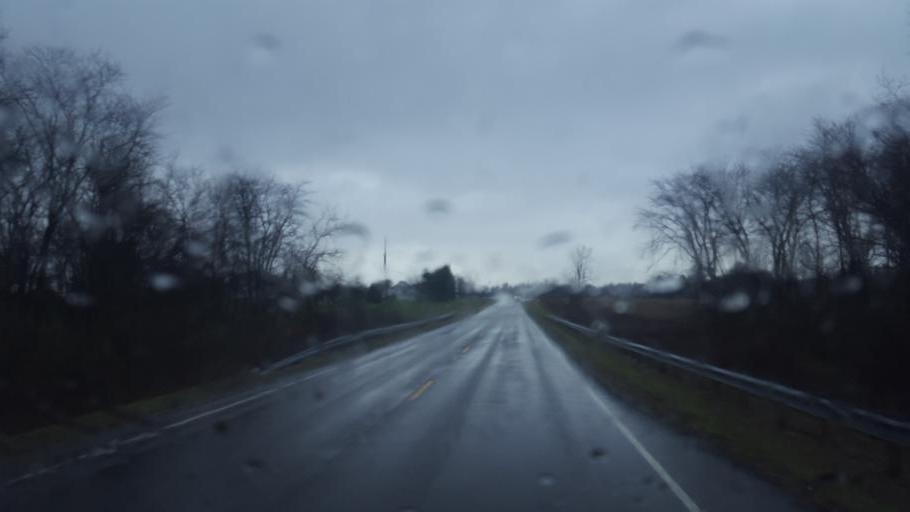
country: US
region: Ohio
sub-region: Delaware County
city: Lewis Center
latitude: 40.2740
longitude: -82.9842
